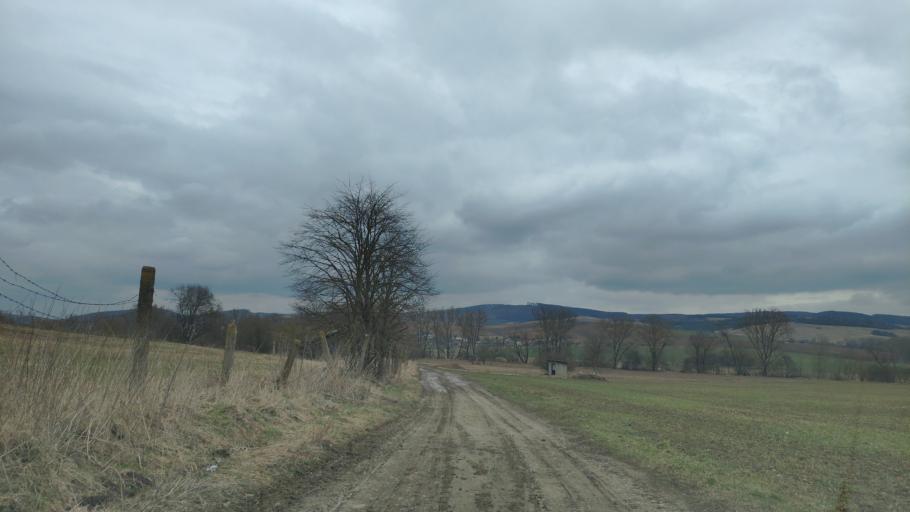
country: SK
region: Presovsky
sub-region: Okres Presov
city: Presov
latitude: 49.0773
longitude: 21.3068
